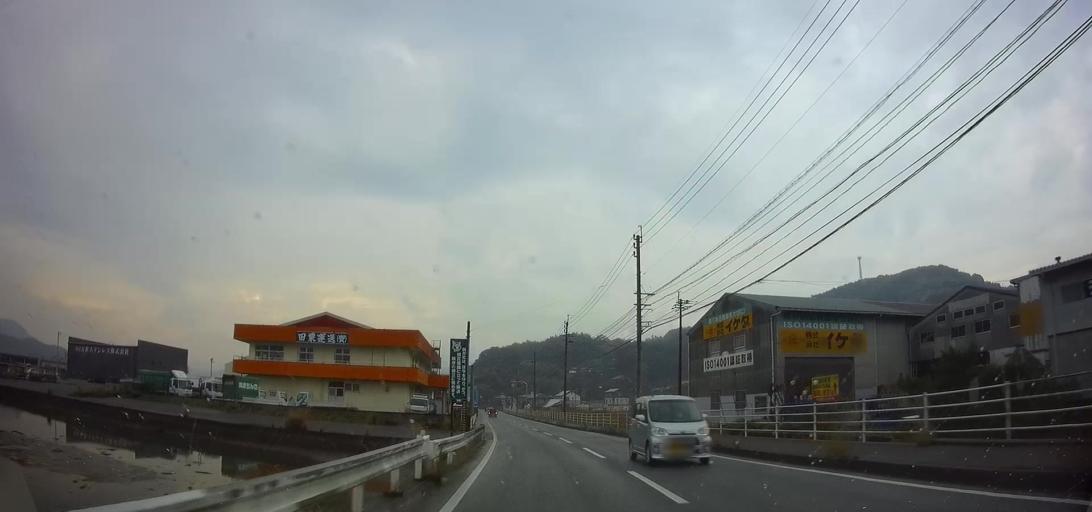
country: JP
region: Nagasaki
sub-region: Isahaya-shi
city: Isahaya
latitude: 32.8494
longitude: 130.0066
